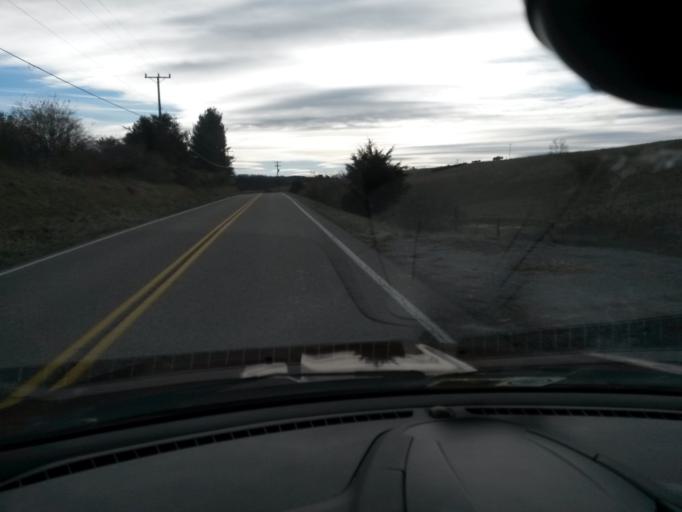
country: US
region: Virginia
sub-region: City of Staunton
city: Staunton
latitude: 38.2417
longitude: -79.1665
